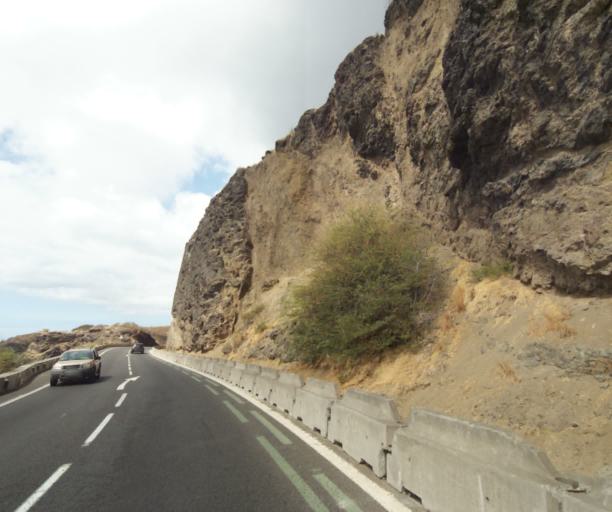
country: RE
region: Reunion
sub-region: Reunion
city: Saint-Paul
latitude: -21.0222
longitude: 55.2323
